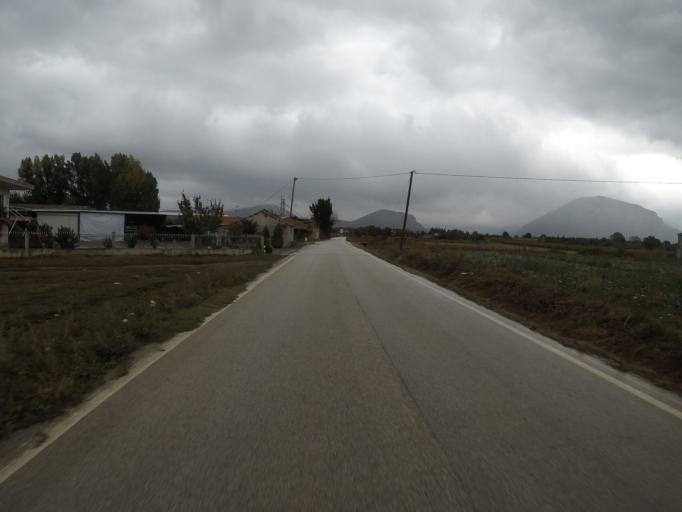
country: GR
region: Peloponnese
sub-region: Nomos Arkadias
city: Tripoli
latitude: 37.5719
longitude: 22.4108
